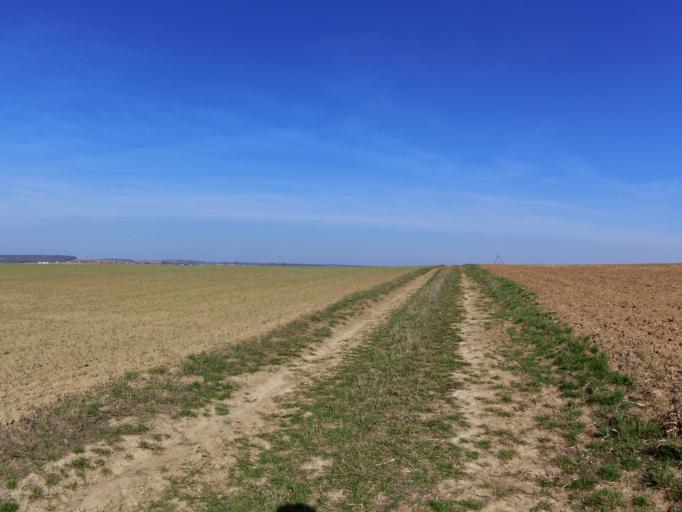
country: DE
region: Bavaria
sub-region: Regierungsbezirk Unterfranken
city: Estenfeld
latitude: 49.8145
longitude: 10.0189
